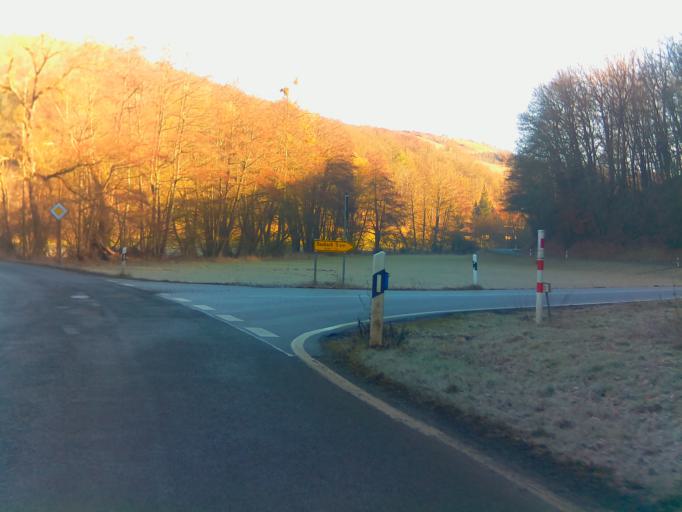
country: DE
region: Rheinland-Pfalz
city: Langenthal
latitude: 49.8235
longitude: 7.5817
